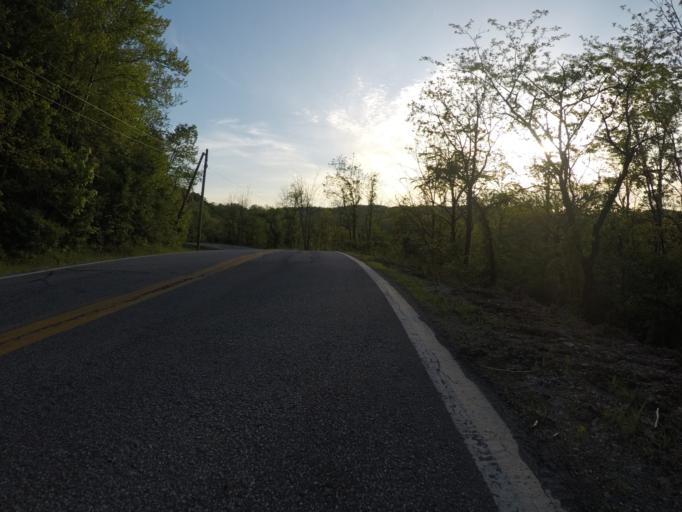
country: US
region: West Virginia
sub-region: Cabell County
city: Huntington
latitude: 38.5234
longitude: -82.4661
